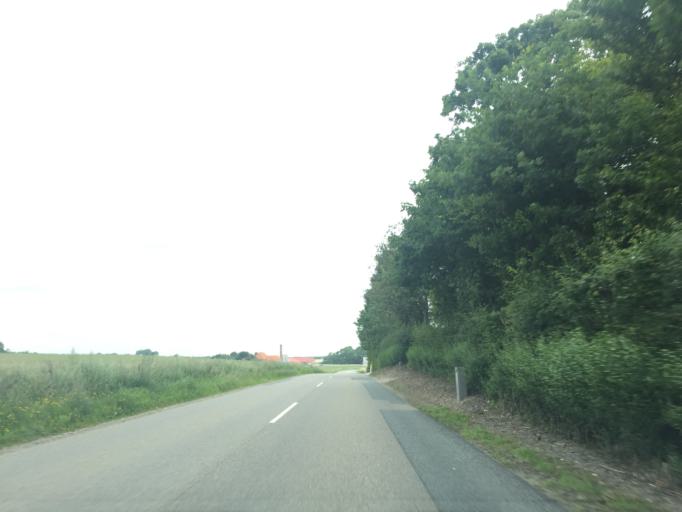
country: DK
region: Central Jutland
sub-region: Favrskov Kommune
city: Ulstrup
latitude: 56.3086
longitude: 9.7621
